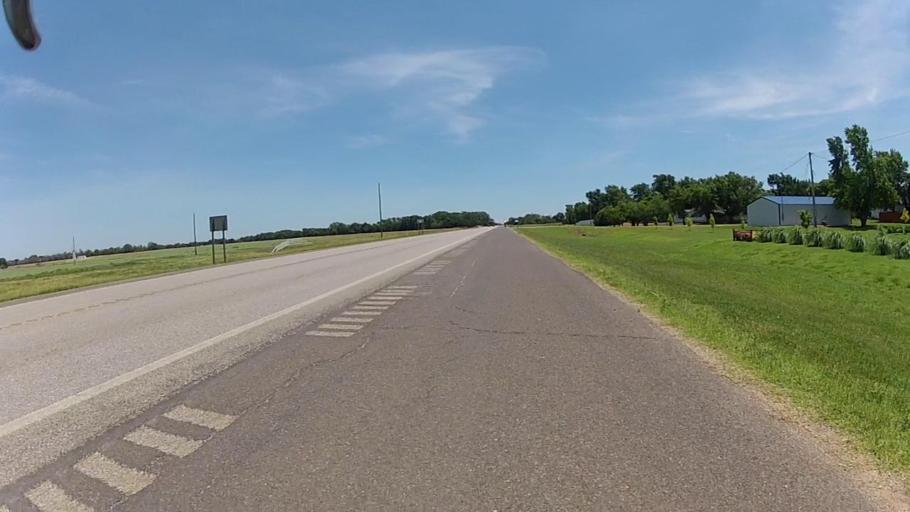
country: US
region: Kansas
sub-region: Barber County
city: Medicine Lodge
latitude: 37.2537
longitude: -98.4177
